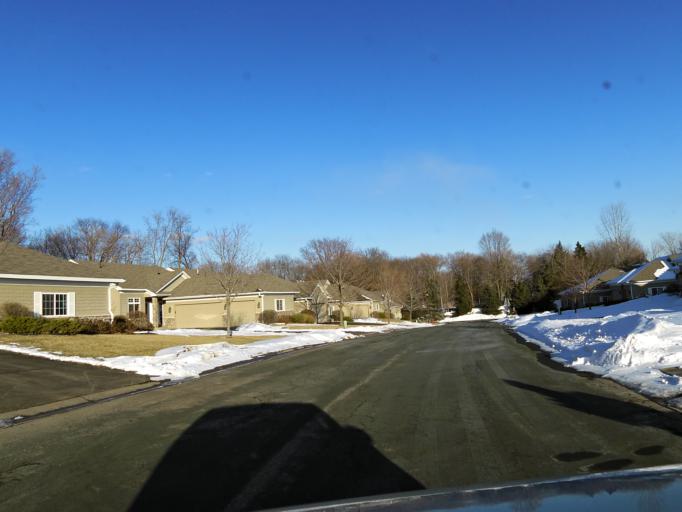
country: US
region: Minnesota
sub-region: Scott County
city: Prior Lake
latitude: 44.7286
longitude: -93.4423
